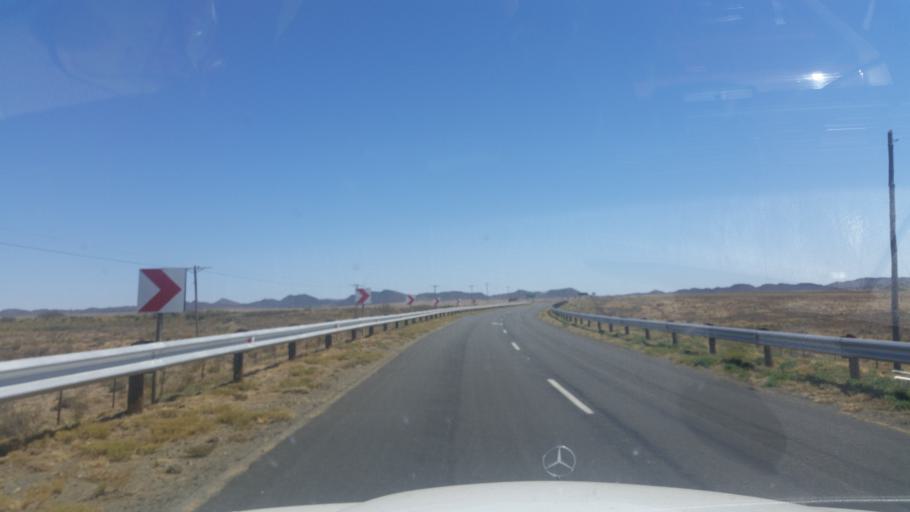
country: ZA
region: Northern Cape
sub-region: Pixley ka Seme District Municipality
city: Colesberg
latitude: -30.7458
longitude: 25.5886
